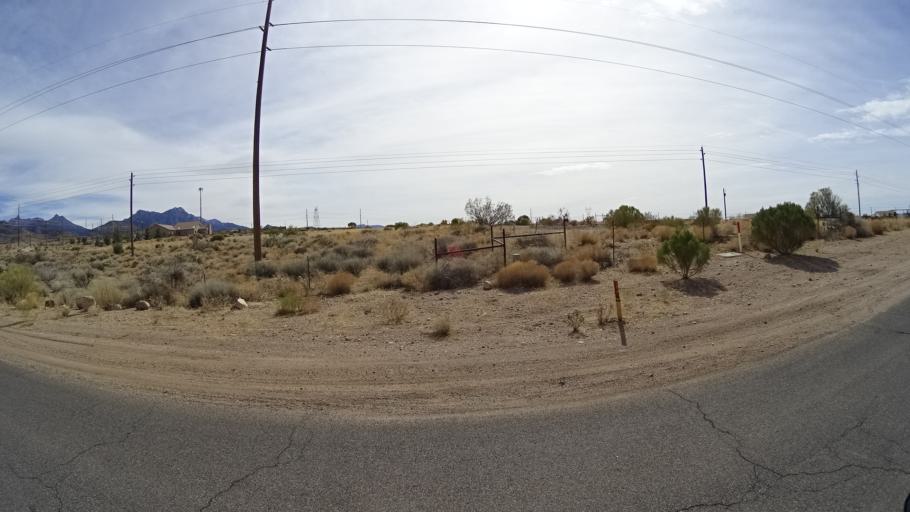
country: US
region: Arizona
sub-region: Mohave County
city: Kingman
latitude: 35.1815
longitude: -113.9838
